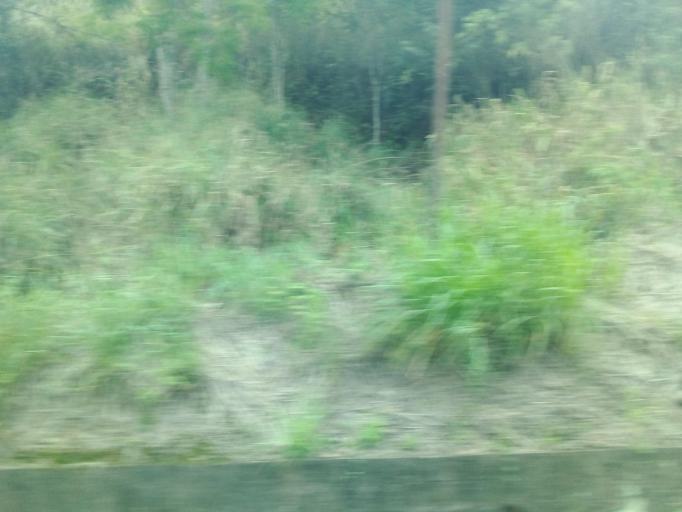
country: BR
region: Minas Gerais
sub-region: Nova Era
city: Nova Era
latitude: -19.7310
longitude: -42.9978
